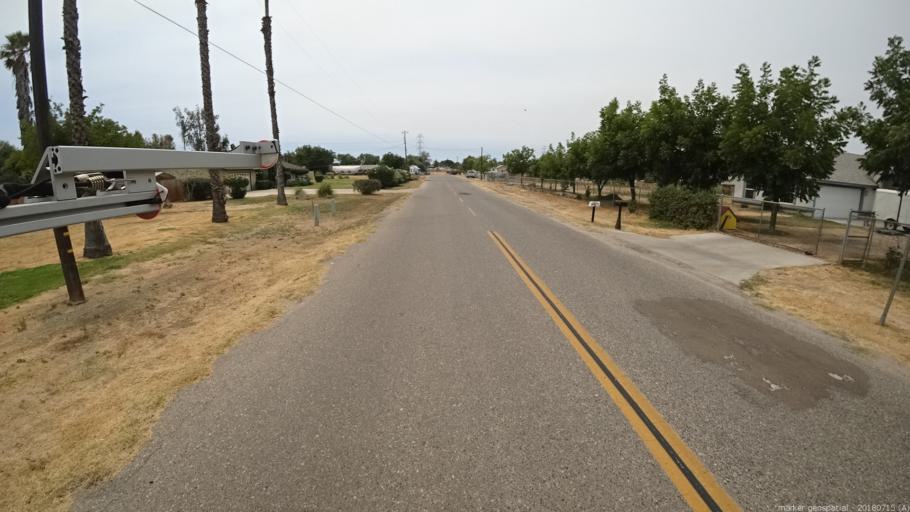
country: US
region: California
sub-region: Madera County
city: Madera Acres
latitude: 37.0140
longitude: -120.0747
